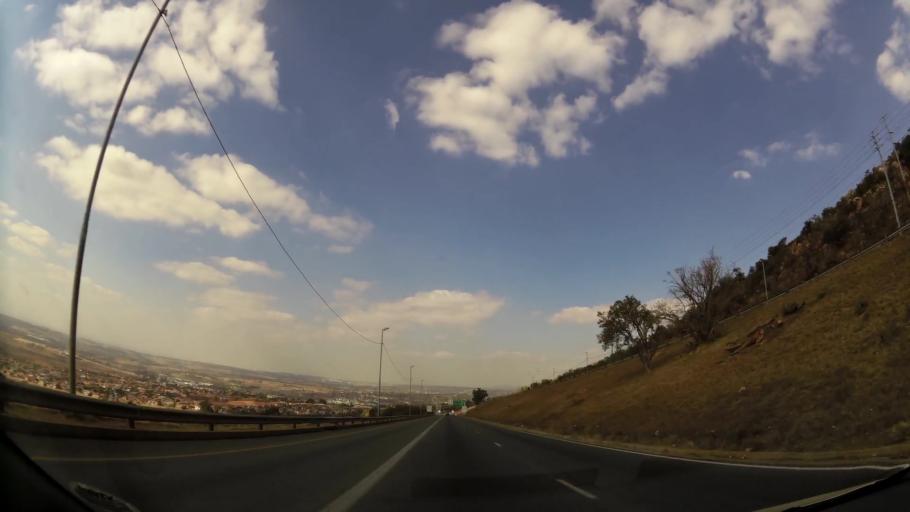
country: ZA
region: Gauteng
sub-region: West Rand District Municipality
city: Muldersdriseloop
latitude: -26.0646
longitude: 27.8138
